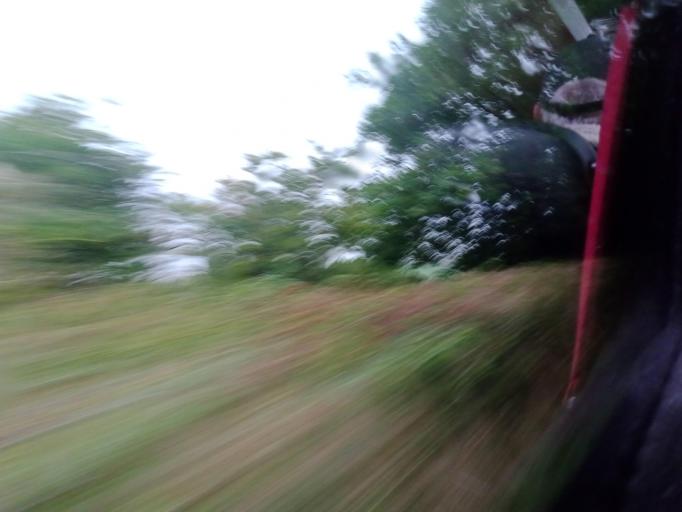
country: IE
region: Munster
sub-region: Waterford
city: Dungarvan
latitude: 52.0513
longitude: -7.6385
